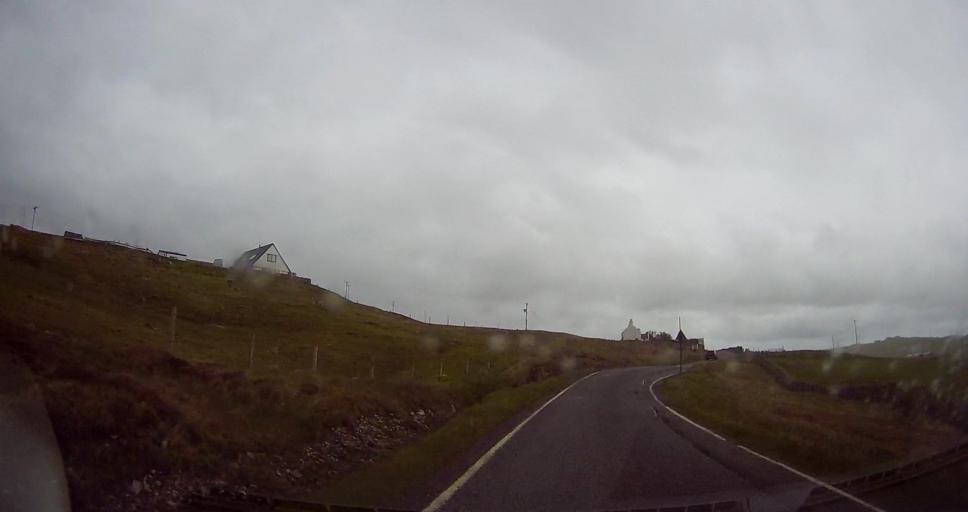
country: GB
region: Scotland
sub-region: Shetland Islands
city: Sandwick
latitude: 60.2445
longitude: -1.5271
